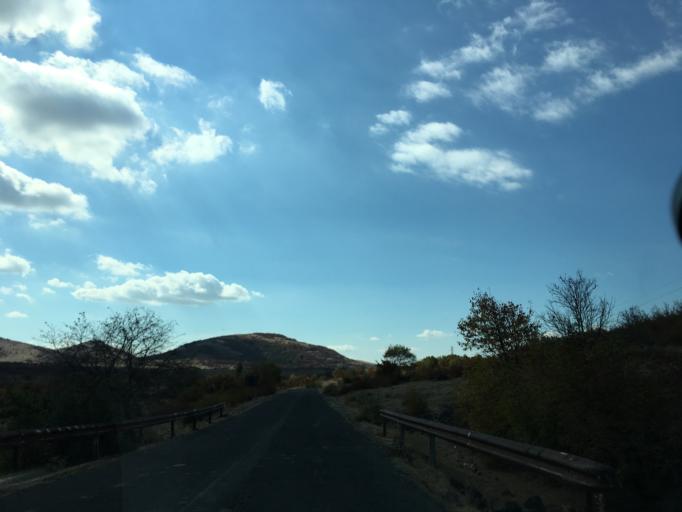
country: BG
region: Kurdzhali
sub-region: Obshtina Kurdzhali
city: Kurdzhali
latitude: 41.5360
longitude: 25.4810
